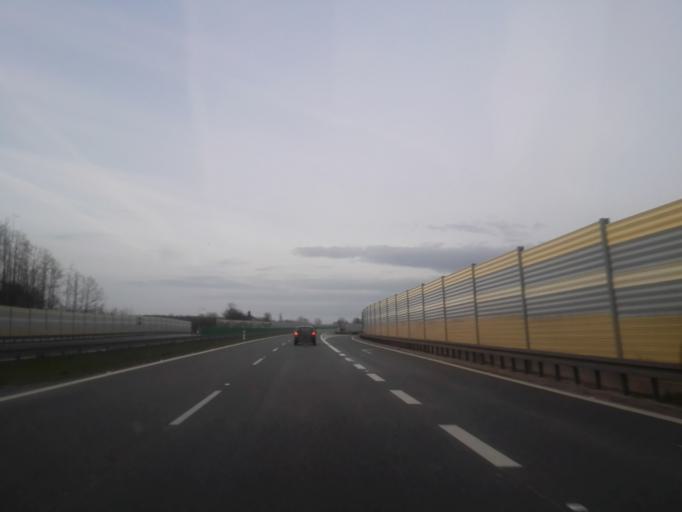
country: PL
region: Masovian Voivodeship
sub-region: Powiat zyrardowski
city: Radziejowice
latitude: 51.9996
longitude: 20.5556
